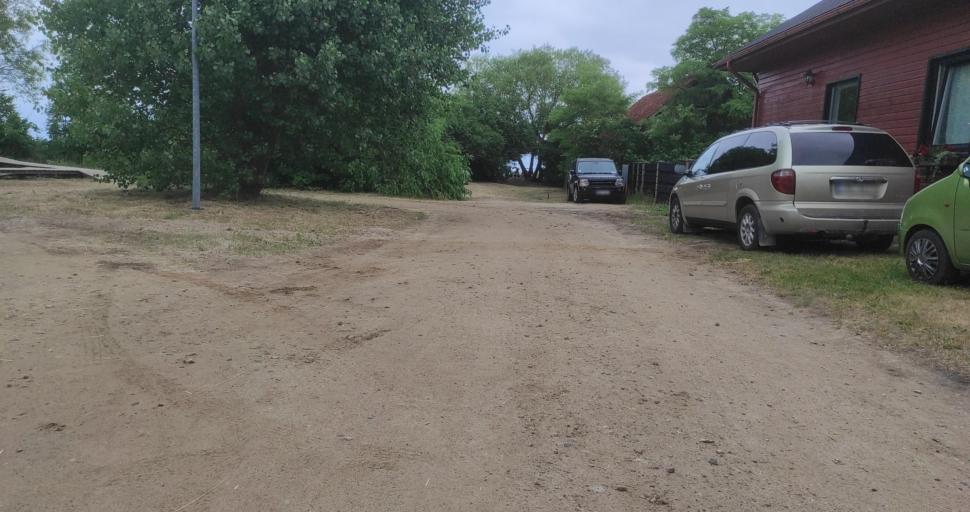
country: LV
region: Pavilostas
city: Pavilosta
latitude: 56.8912
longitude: 21.1778
